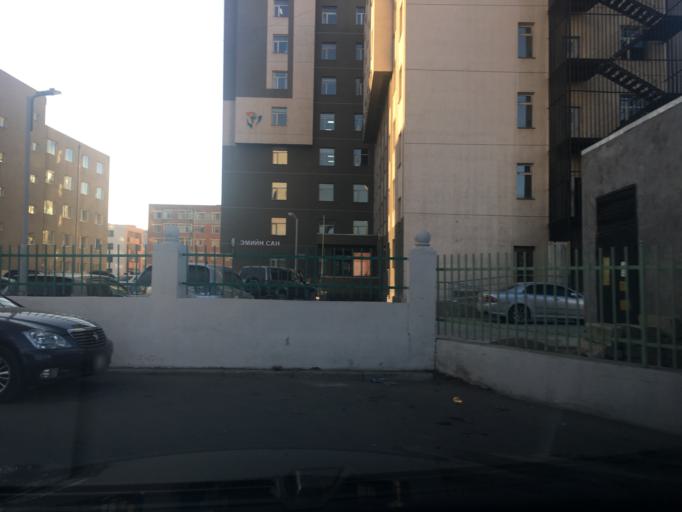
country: MN
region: Ulaanbaatar
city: Ulaanbaatar
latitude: 47.9200
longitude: 106.8852
